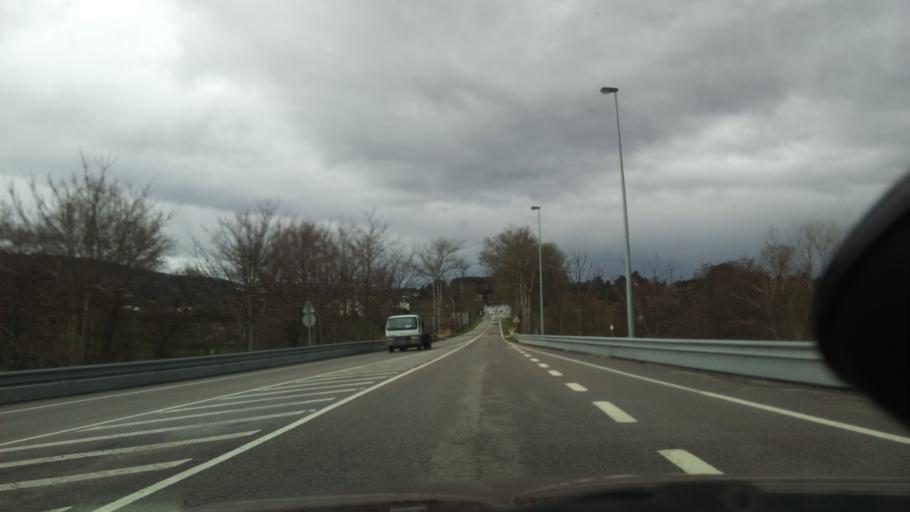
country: PT
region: Guarda
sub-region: Fornos de Algodres
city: Fornos de Algodres
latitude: 40.5341
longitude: -7.5729
